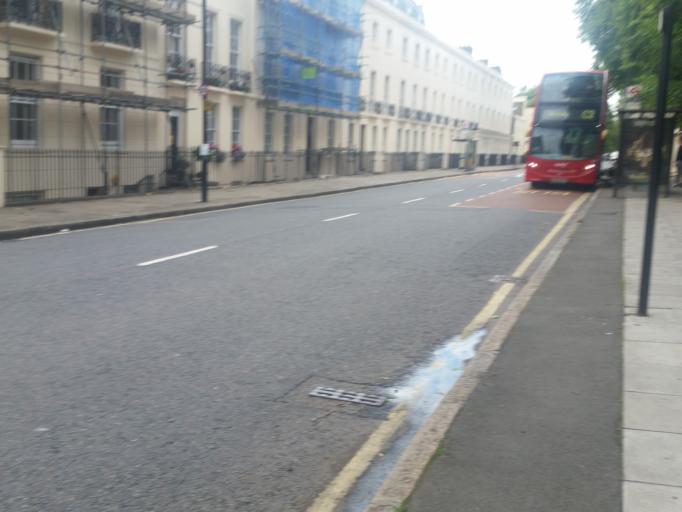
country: GB
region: England
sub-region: Greater London
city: Camden Town
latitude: 51.5342
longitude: -0.1463
